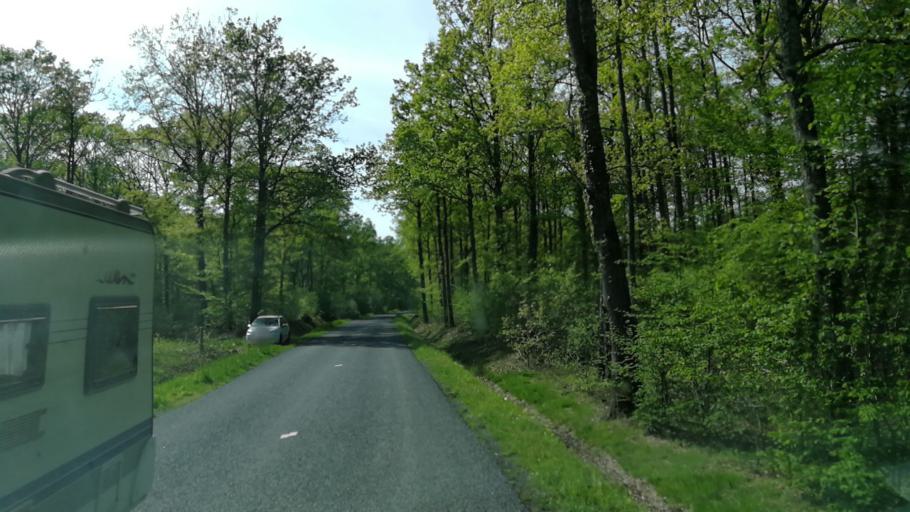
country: FR
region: Auvergne
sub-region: Departement de l'Allier
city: Neuilly-le-Real
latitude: 46.5162
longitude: 3.4434
